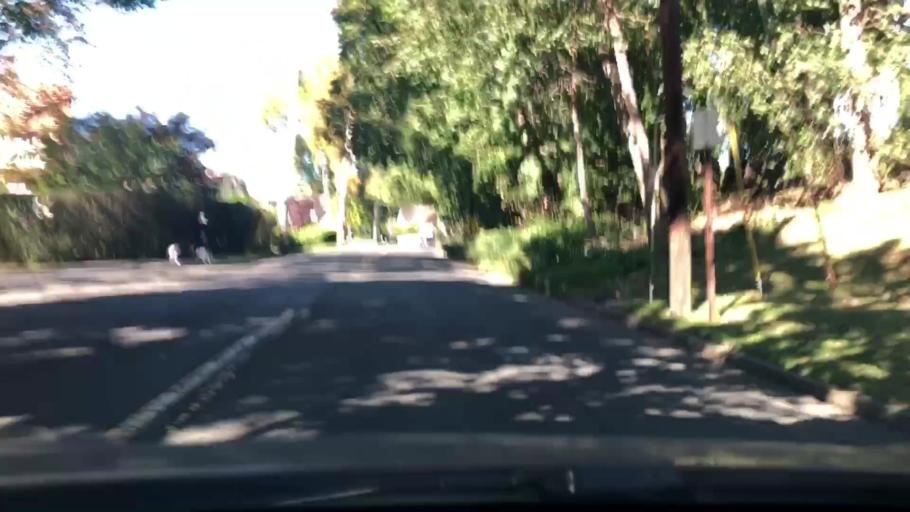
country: US
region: New York
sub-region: Westchester County
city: Bronxville
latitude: 40.9284
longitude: -73.8210
